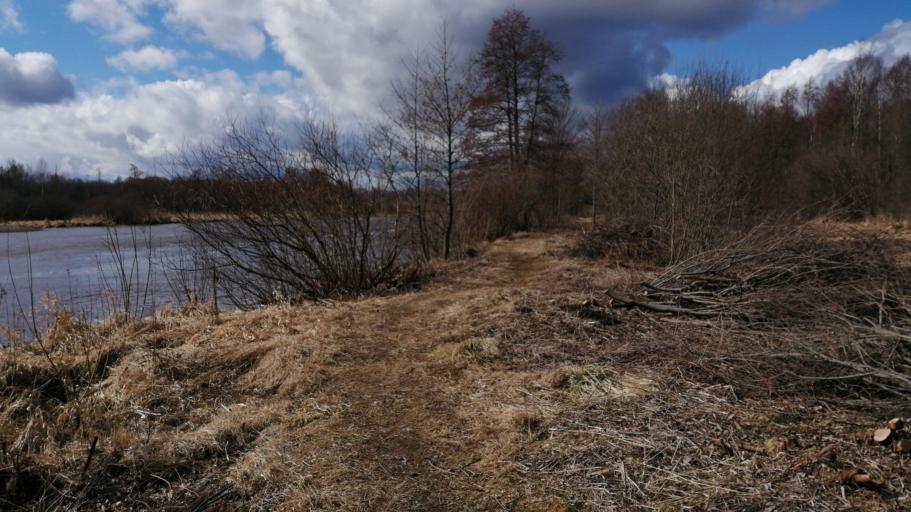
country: EE
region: Tartu
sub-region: Alatskivi vald
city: Kallaste
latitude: 58.3833
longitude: 27.1193
